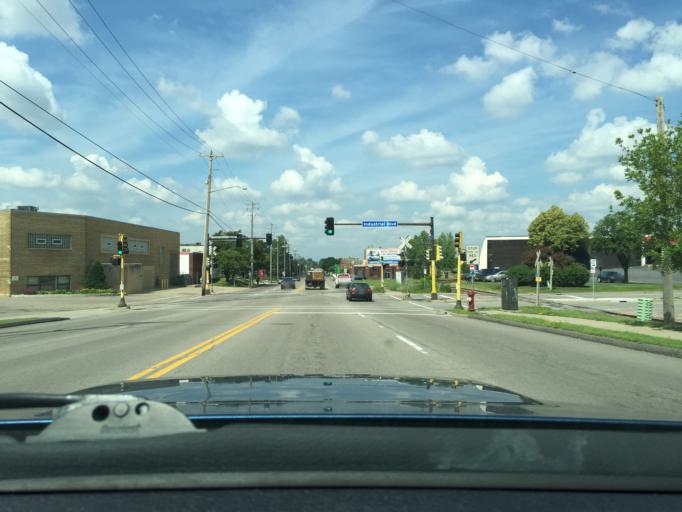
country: US
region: Minnesota
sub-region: Ramsey County
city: Lauderdale
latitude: 44.9917
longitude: -93.2094
